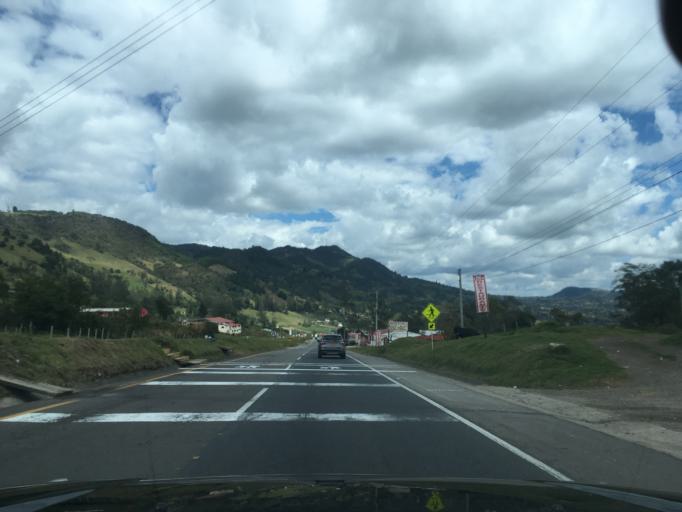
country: CO
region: Boyaca
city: Ventaquemada
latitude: 5.3620
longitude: -73.5330
